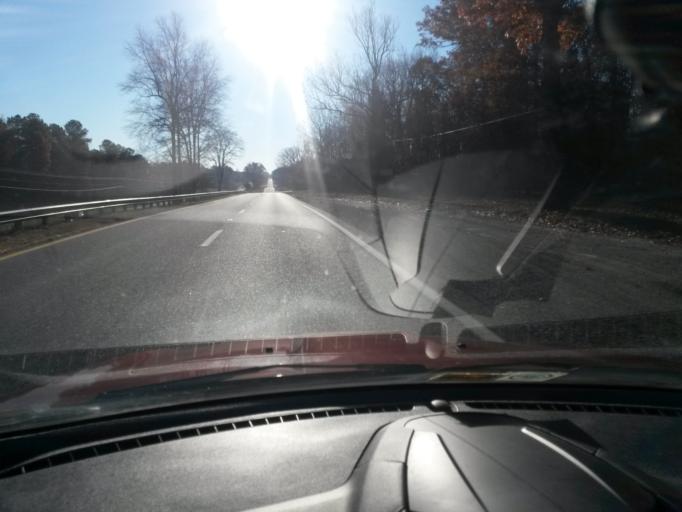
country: US
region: Virginia
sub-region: Appomattox County
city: Appomattox
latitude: 37.3030
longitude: -78.7469
